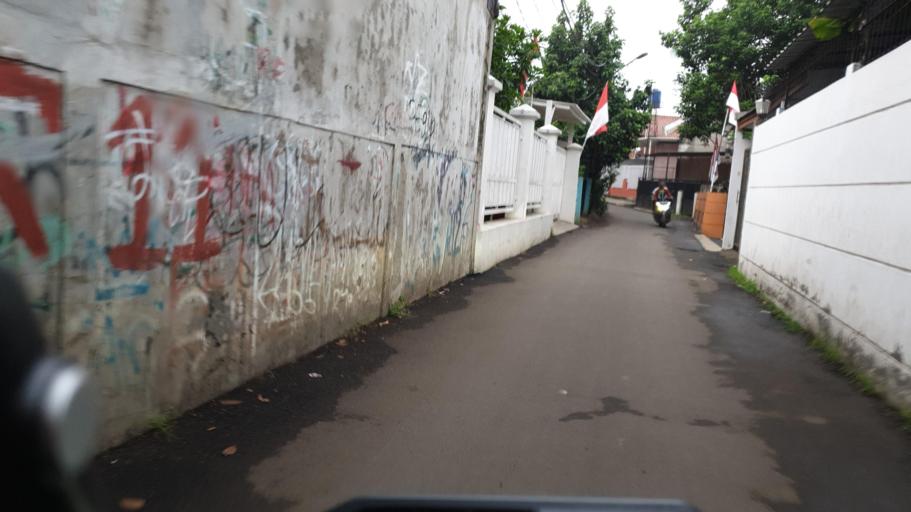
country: ID
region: West Java
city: Pamulang
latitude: -6.3305
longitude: 106.7732
